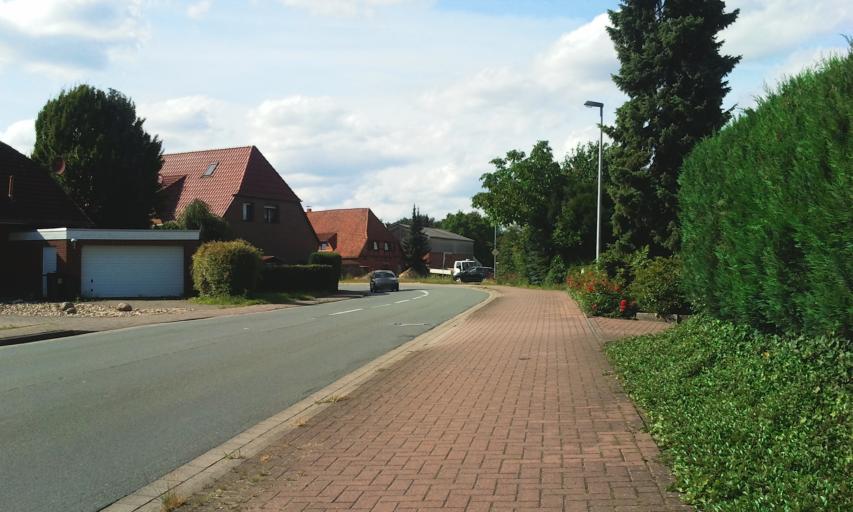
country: DE
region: Lower Saxony
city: Drakenburg
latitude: 52.6746
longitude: 9.2310
